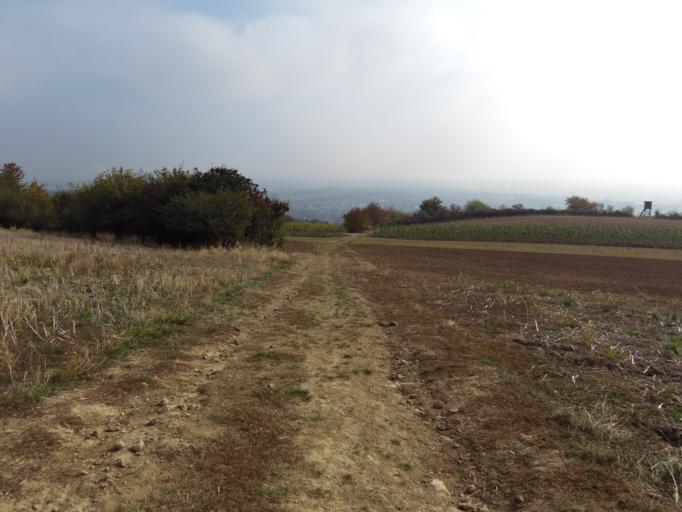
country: DE
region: Rheinland-Pfalz
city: Mertesheim
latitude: 49.5824
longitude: 8.1444
